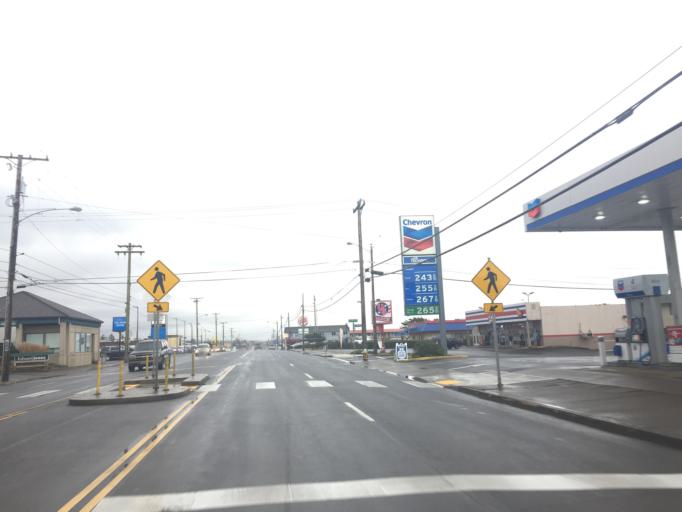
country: US
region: Oregon
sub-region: Lincoln County
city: Newport
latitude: 44.6488
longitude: -124.0531
